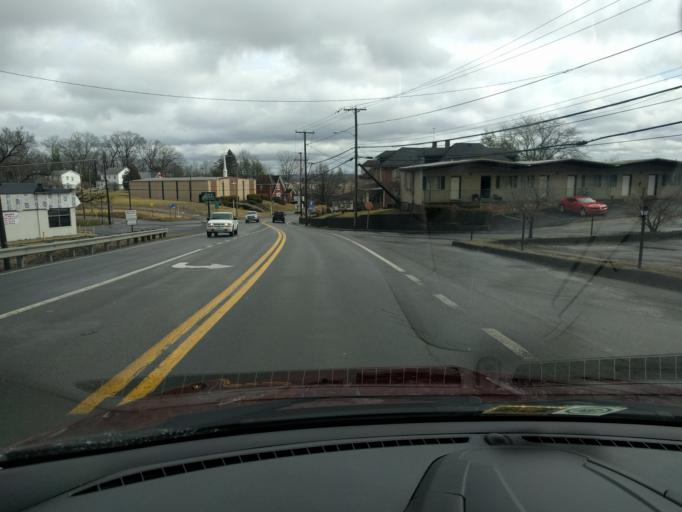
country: US
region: West Virginia
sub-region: Raleigh County
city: Mabscott
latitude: 37.7775
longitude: -81.1996
